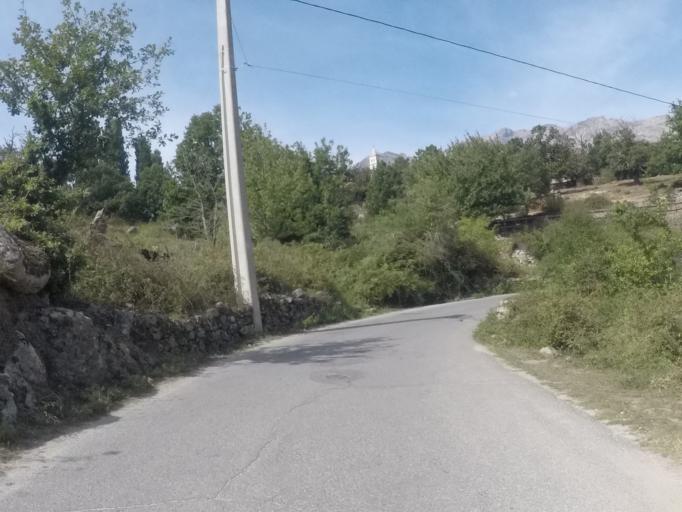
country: FR
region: Corsica
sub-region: Departement de la Haute-Corse
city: Corte
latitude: 42.3348
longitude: 9.0155
